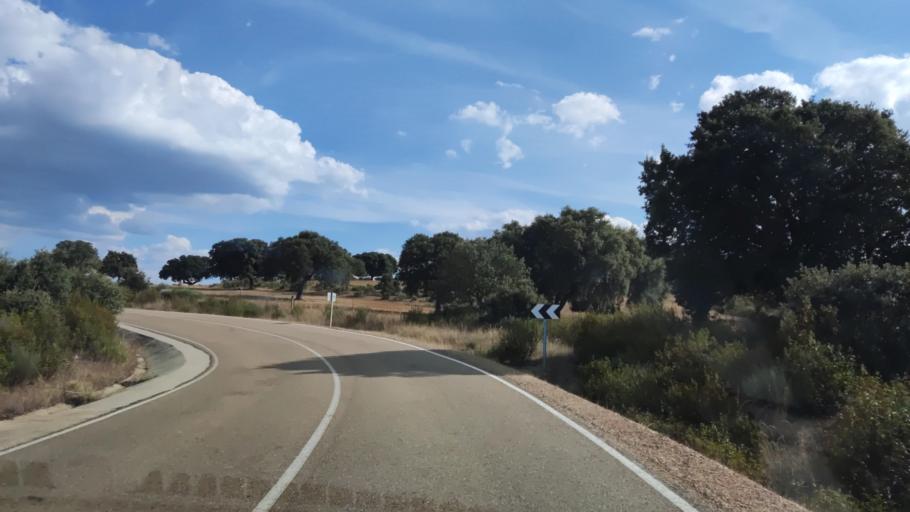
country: ES
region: Castille and Leon
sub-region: Provincia de Salamanca
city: Pastores
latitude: 40.5224
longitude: -6.5194
